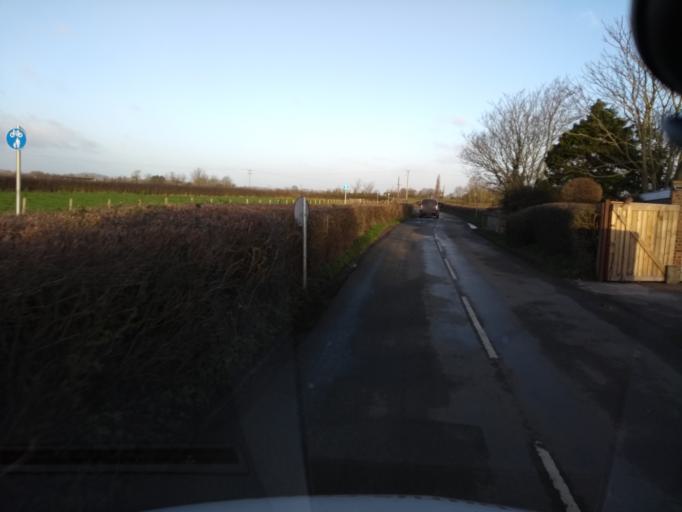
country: GB
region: England
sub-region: Somerset
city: Bridgwater
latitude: 51.1432
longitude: -3.0049
